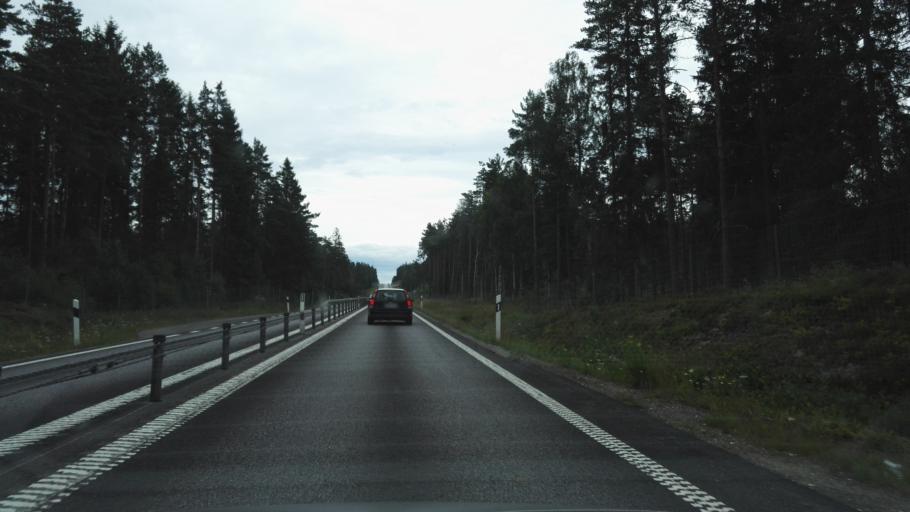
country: SE
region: Kronoberg
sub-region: Vaxjo Kommun
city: Rottne
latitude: 56.9493
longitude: 14.9245
